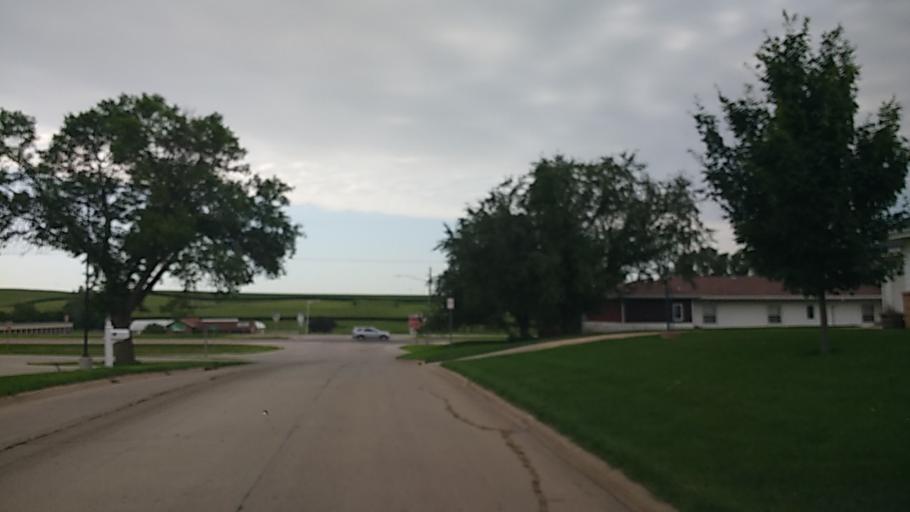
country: US
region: Iowa
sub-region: Woodbury County
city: Moville
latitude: 42.4828
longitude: -96.0653
